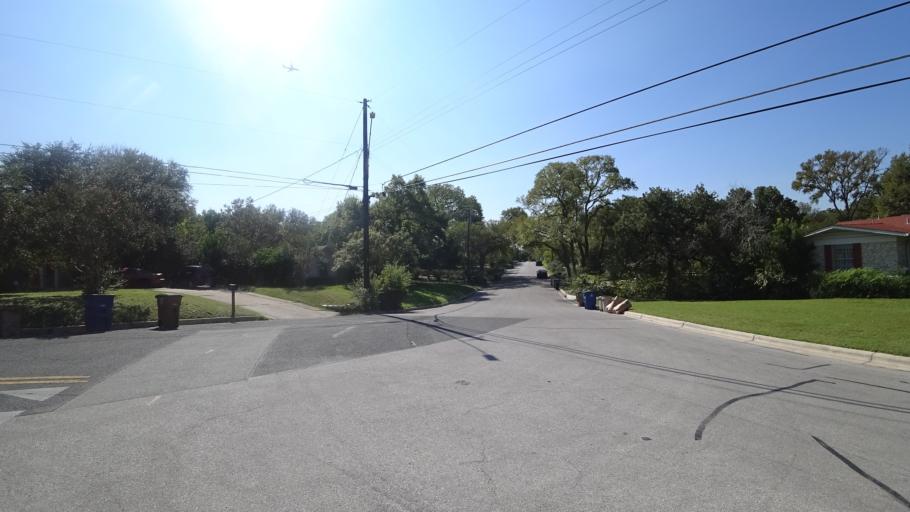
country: US
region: Texas
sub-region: Travis County
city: Austin
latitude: 30.3096
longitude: -97.6760
